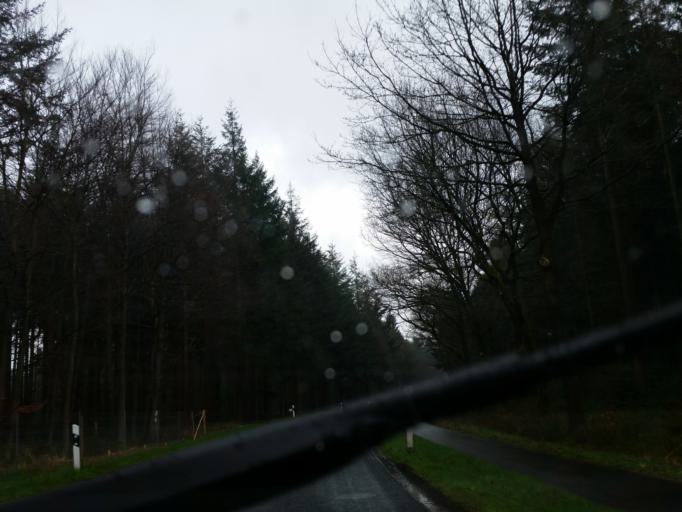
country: DE
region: Lower Saxony
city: Hipstedt
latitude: 53.5012
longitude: 8.9934
